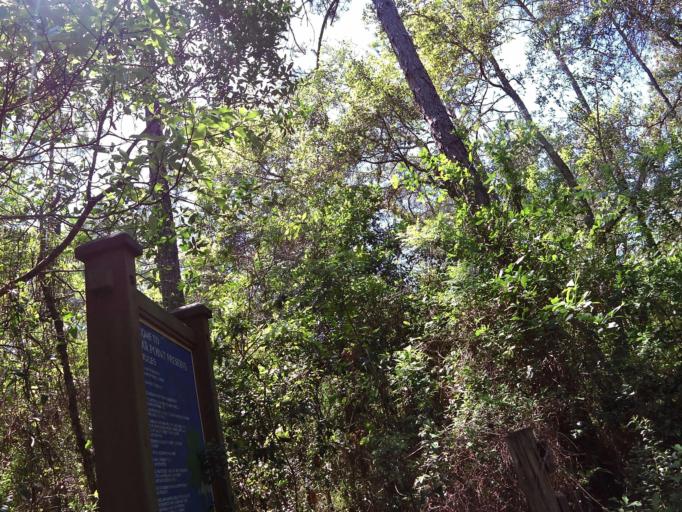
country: US
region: Florida
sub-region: Duval County
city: Atlantic Beach
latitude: 30.4567
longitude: -81.4865
